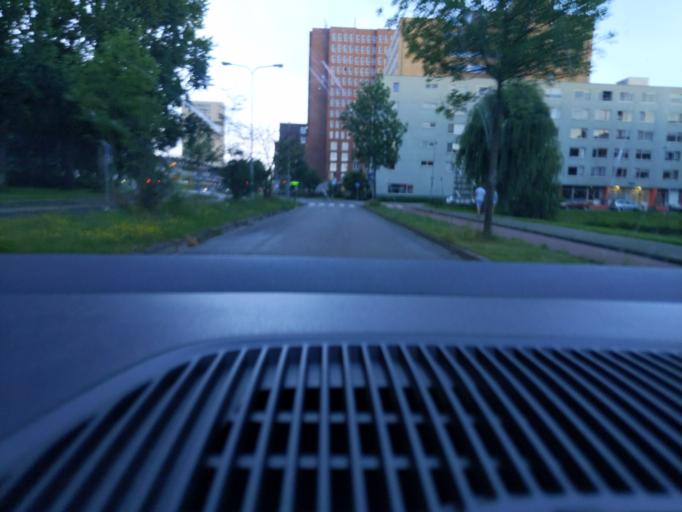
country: NL
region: Groningen
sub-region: Gemeente Groningen
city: Korrewegwijk
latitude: 53.2322
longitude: 6.5404
